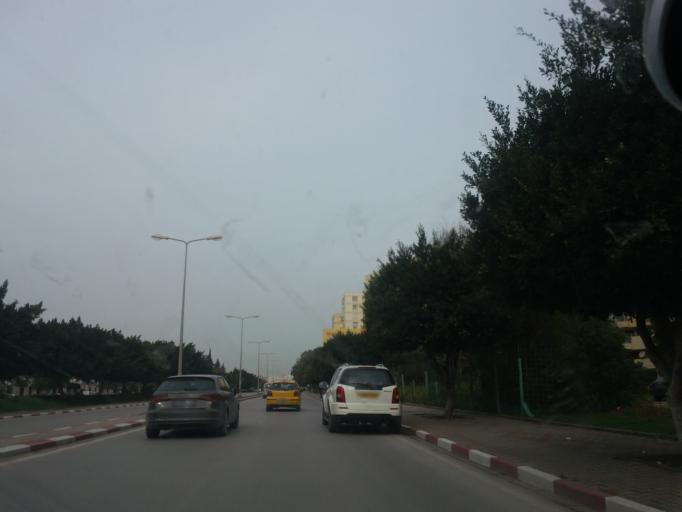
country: TN
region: Tunis
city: Tunis
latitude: 36.8452
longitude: 10.1628
